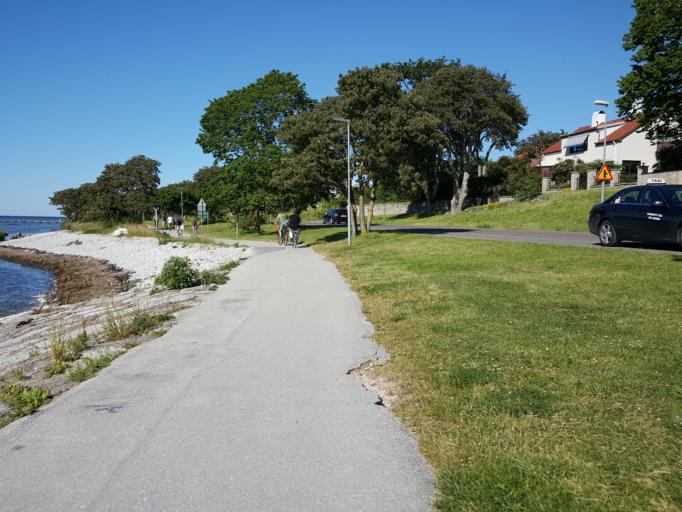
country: SE
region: Gotland
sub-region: Gotland
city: Visby
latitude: 57.6503
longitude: 18.3008
